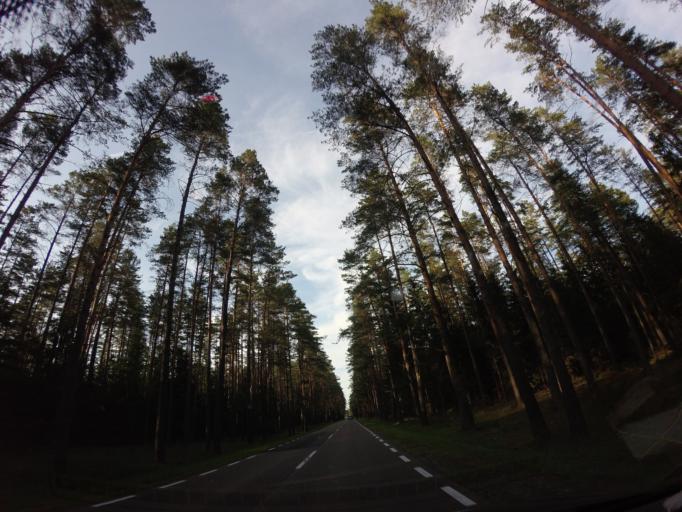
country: PL
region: Podlasie
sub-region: Powiat augustowski
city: Augustow
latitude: 53.8970
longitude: 23.1251
